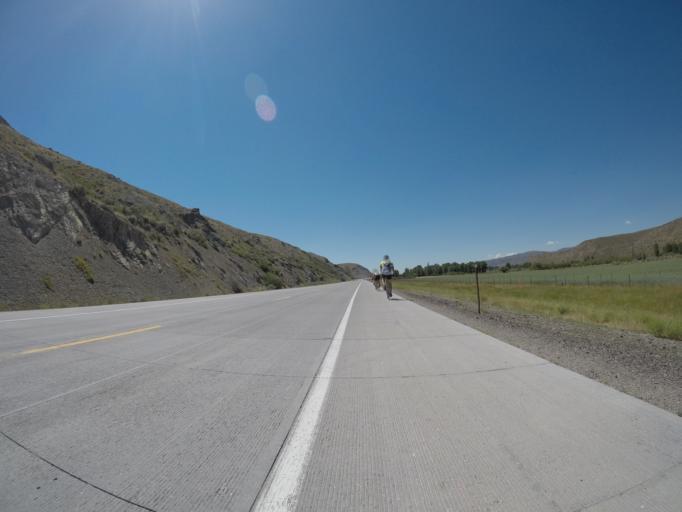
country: US
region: Idaho
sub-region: Bear Lake County
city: Montpelier
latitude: 42.1341
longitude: -110.9690
